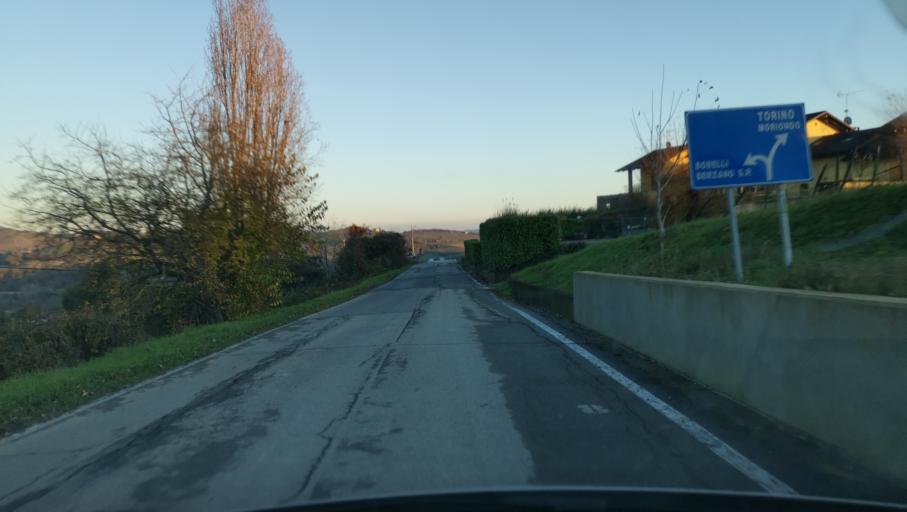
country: IT
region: Piedmont
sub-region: Provincia di Asti
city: Moncucco Torinese
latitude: 45.0626
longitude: 7.9344
